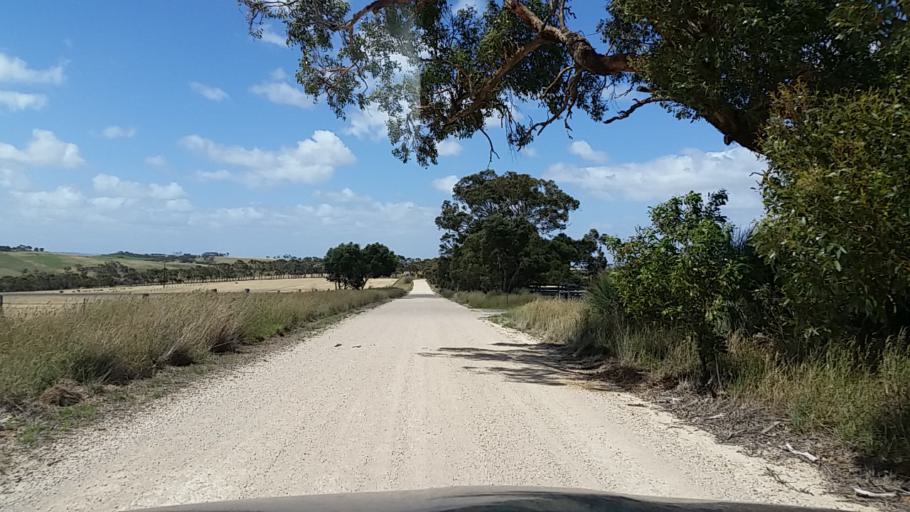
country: AU
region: South Australia
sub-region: Alexandrina
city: Port Elliot
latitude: -35.4521
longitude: 138.6461
